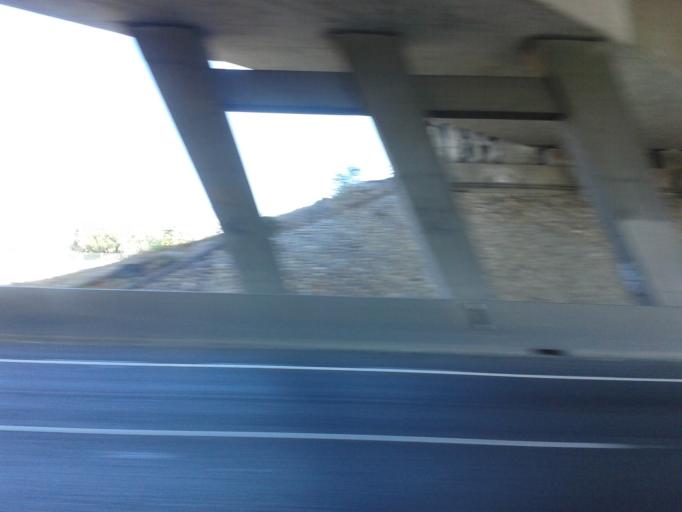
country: ES
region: Madrid
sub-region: Provincia de Madrid
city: Torrejon de Ardoz
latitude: 40.4667
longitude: -3.4557
